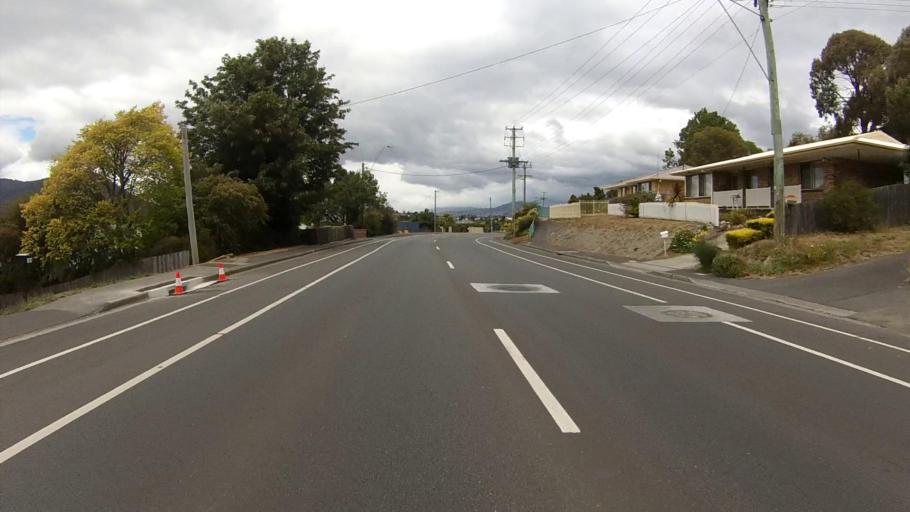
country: AU
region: Tasmania
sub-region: Glenorchy
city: Claremont
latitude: -42.7775
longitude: 147.2514
